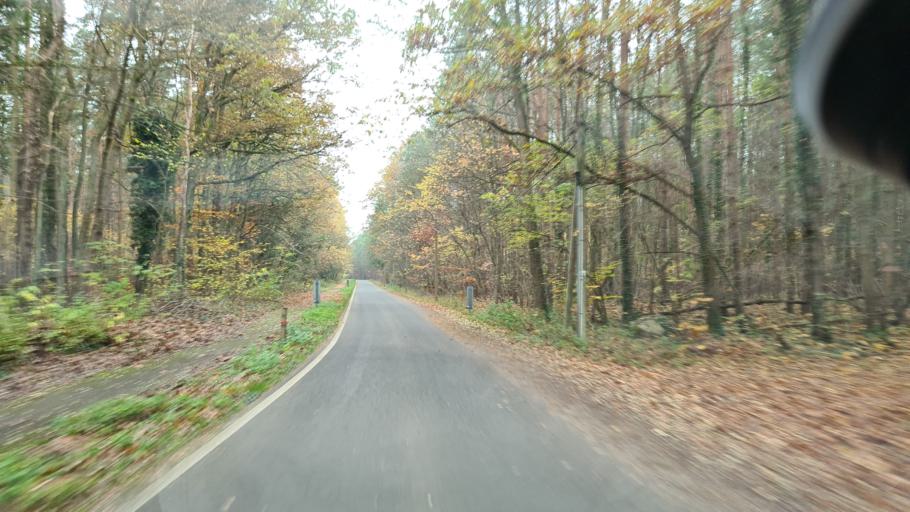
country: DE
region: Brandenburg
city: Lindow
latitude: 52.9928
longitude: 12.9667
